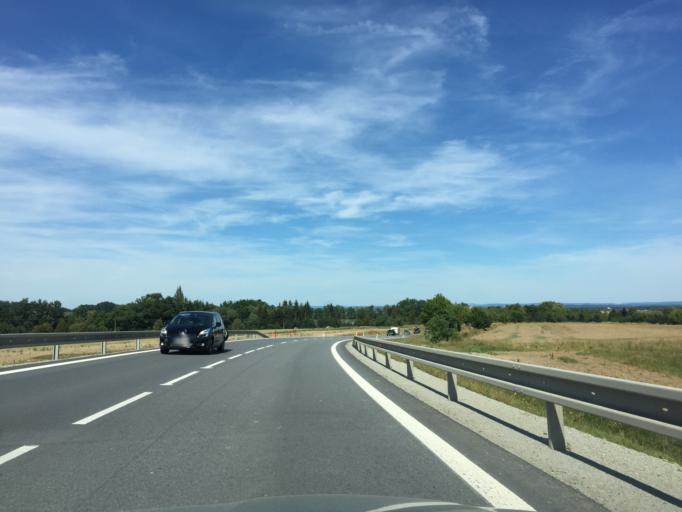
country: CZ
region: Jihocesky
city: Sevetin
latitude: 49.1141
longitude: 14.5839
